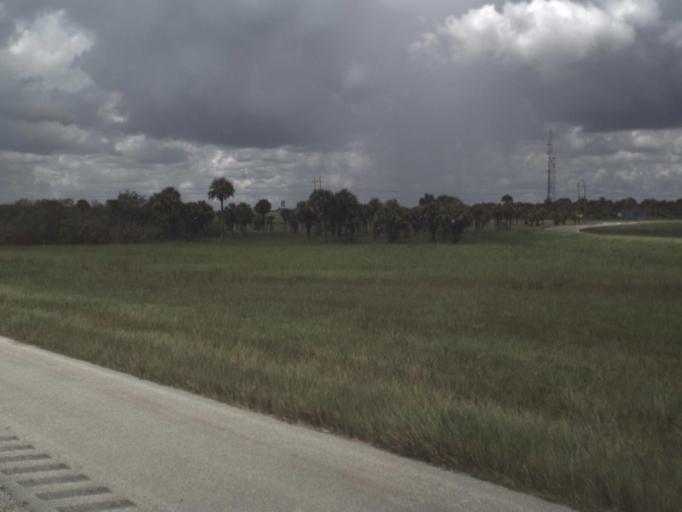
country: US
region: Florida
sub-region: Collier County
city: Immokalee
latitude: 26.1549
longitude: -81.3422
